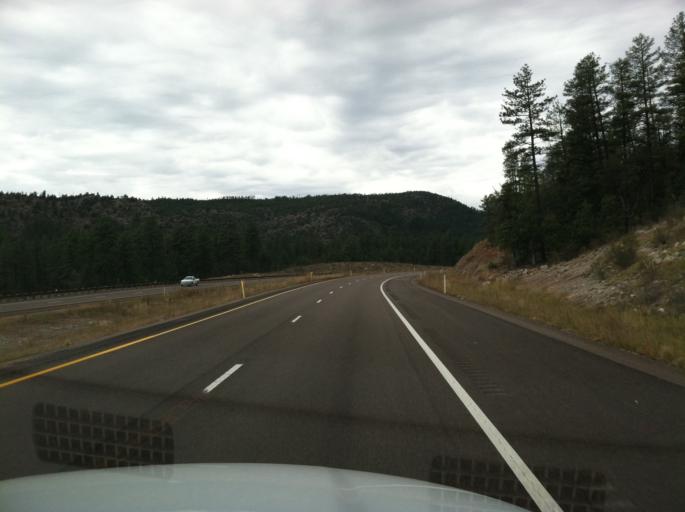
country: US
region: Arizona
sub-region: Gila County
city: Star Valley
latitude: 34.3127
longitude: -111.0402
